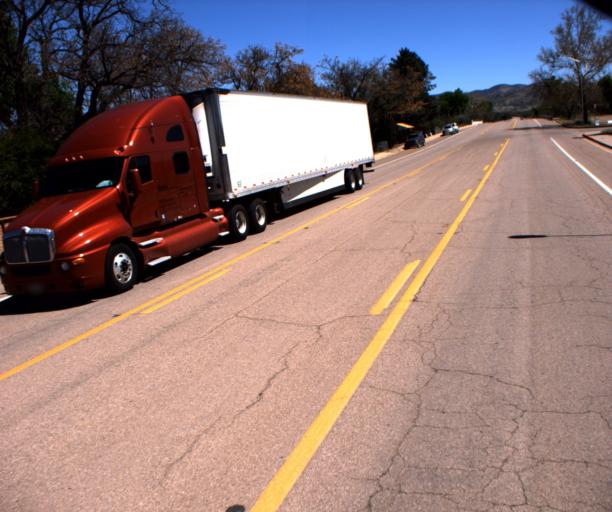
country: US
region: Arizona
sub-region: Santa Cruz County
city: Rio Rico
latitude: 31.5412
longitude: -110.7526
